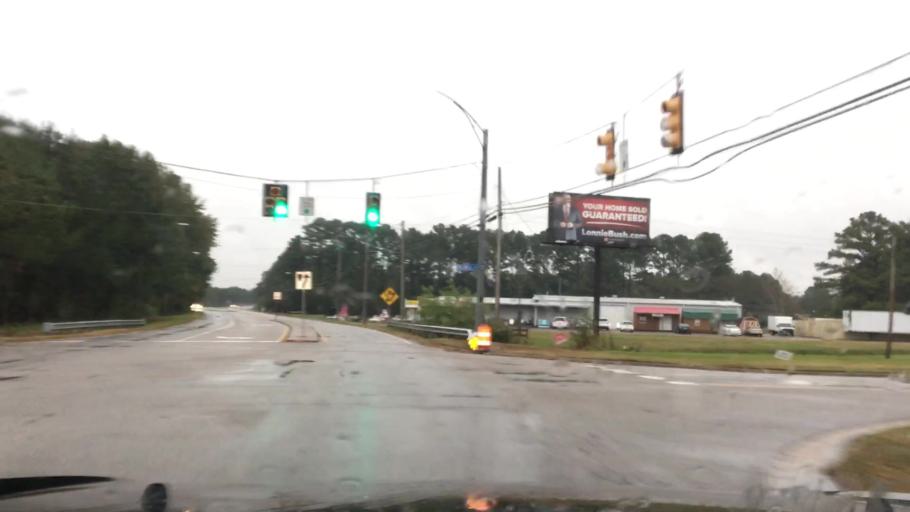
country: US
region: Virginia
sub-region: City of Chesapeake
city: Chesapeake
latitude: 36.6759
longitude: -76.2267
